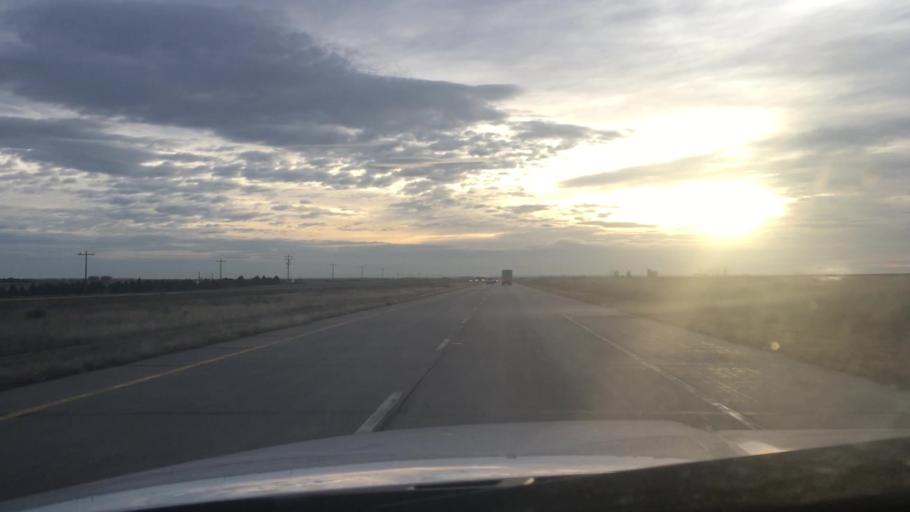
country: US
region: Colorado
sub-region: Morgan County
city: Fort Morgan
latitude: 40.2498
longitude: -104.0128
